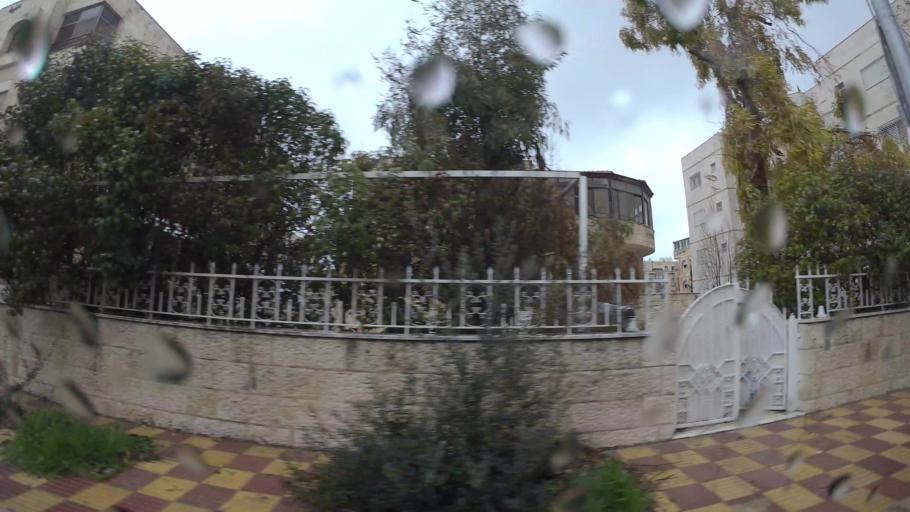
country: JO
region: Amman
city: Al Jubayhah
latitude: 32.0280
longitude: 35.8725
